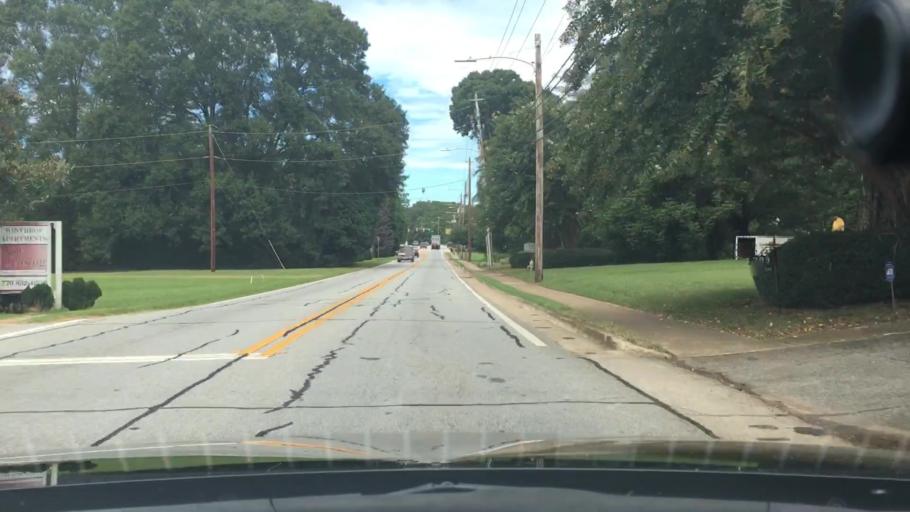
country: US
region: Georgia
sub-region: Coweta County
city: Newnan
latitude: 33.3902
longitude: -84.8013
